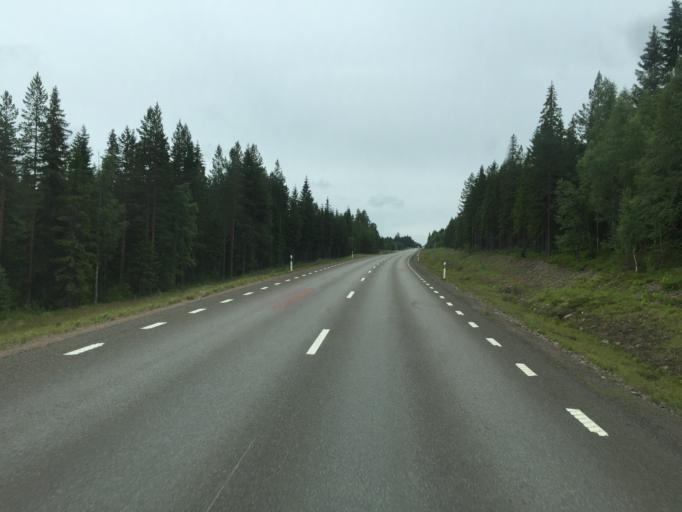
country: SE
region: Dalarna
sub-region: Malung-Saelens kommun
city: Malung
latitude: 60.5857
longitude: 13.5804
